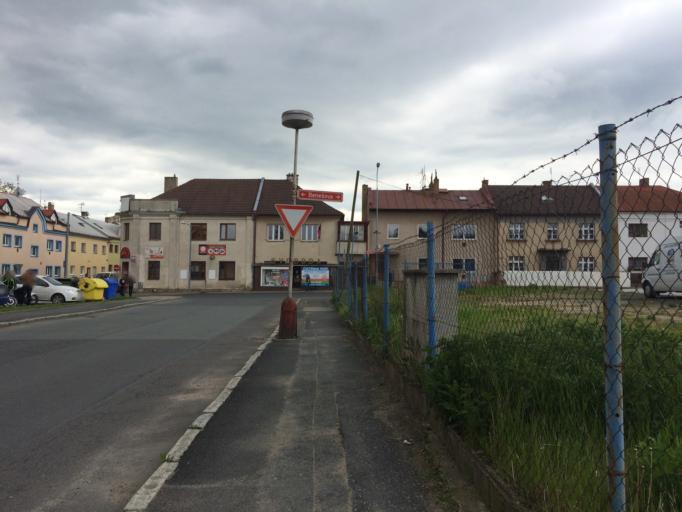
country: CZ
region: Central Bohemia
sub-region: Okres Kutna Hora
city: Kutna Hora
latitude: 49.9574
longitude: 15.2770
